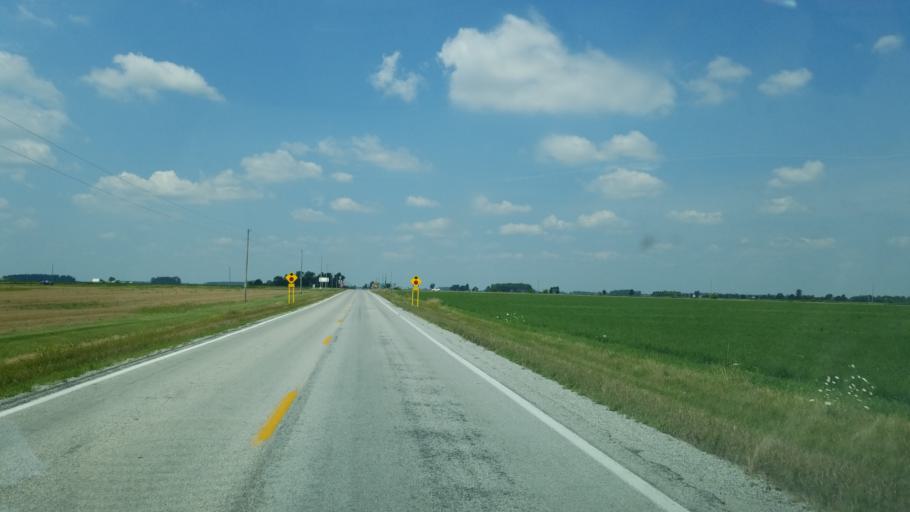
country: US
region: Ohio
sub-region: Henry County
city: Deshler
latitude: 41.2839
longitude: -83.9372
